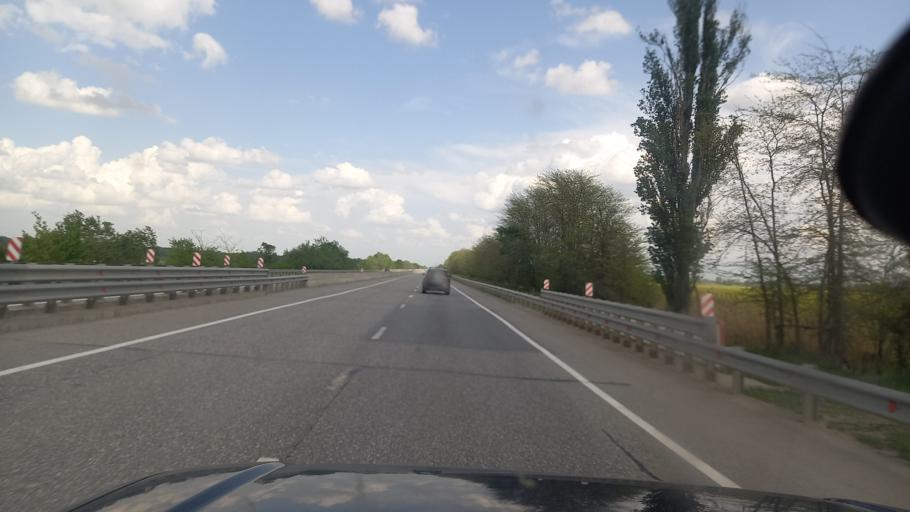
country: RU
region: Chechnya
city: Samashki
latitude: 43.2432
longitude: 45.2979
